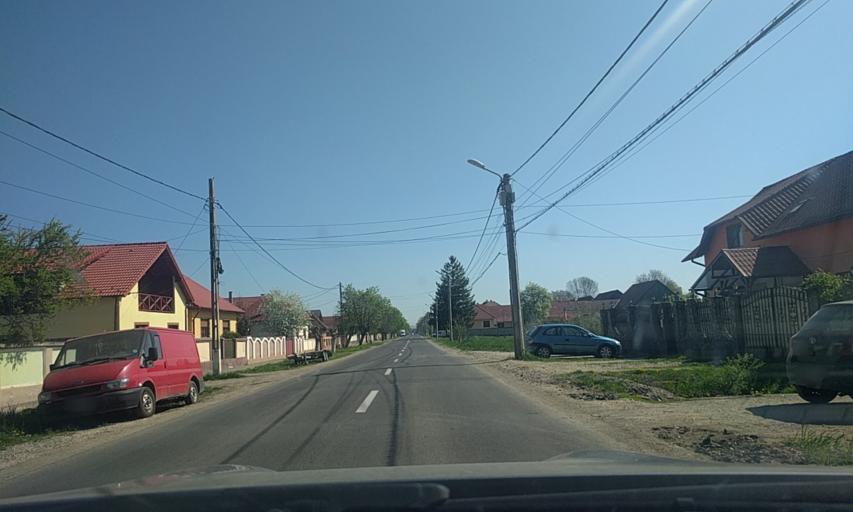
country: RO
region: Brasov
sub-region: Comuna Bod
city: Colonia Bod
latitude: 45.7000
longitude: 25.5619
